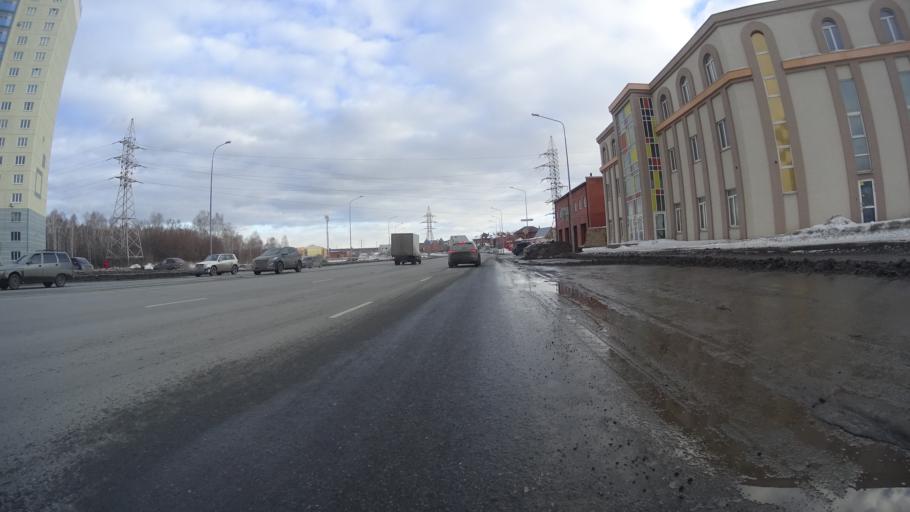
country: RU
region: Chelyabinsk
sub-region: Gorod Chelyabinsk
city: Chelyabinsk
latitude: 55.1579
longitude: 61.3054
